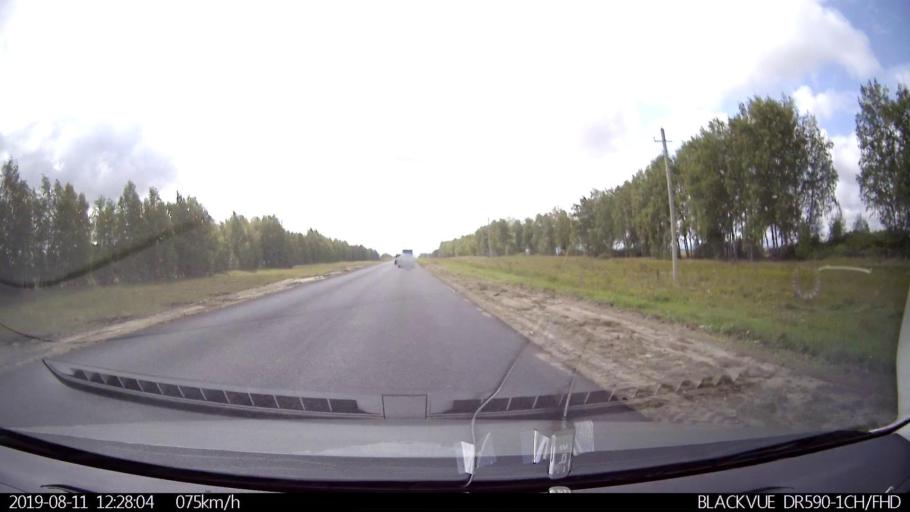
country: RU
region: Ulyanovsk
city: Ignatovka
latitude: 53.8476
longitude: 47.9148
